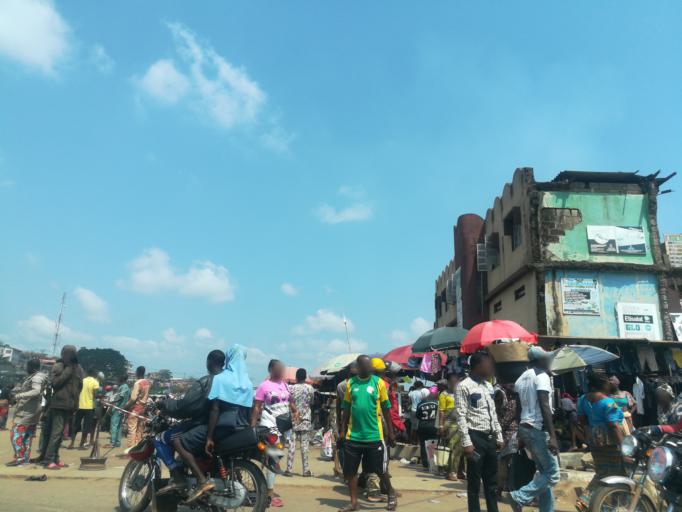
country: NG
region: Ogun
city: Abeokuta
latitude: 7.1559
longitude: 3.3263
